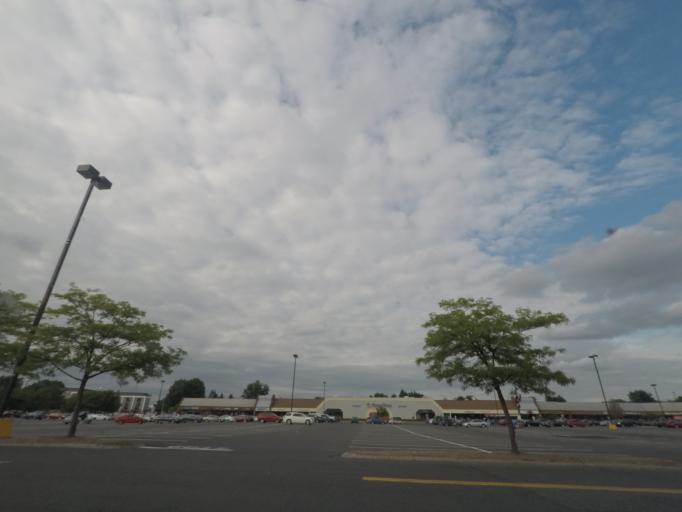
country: US
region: Massachusetts
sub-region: Hampden County
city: West Springfield
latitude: 42.1294
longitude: -72.6238
